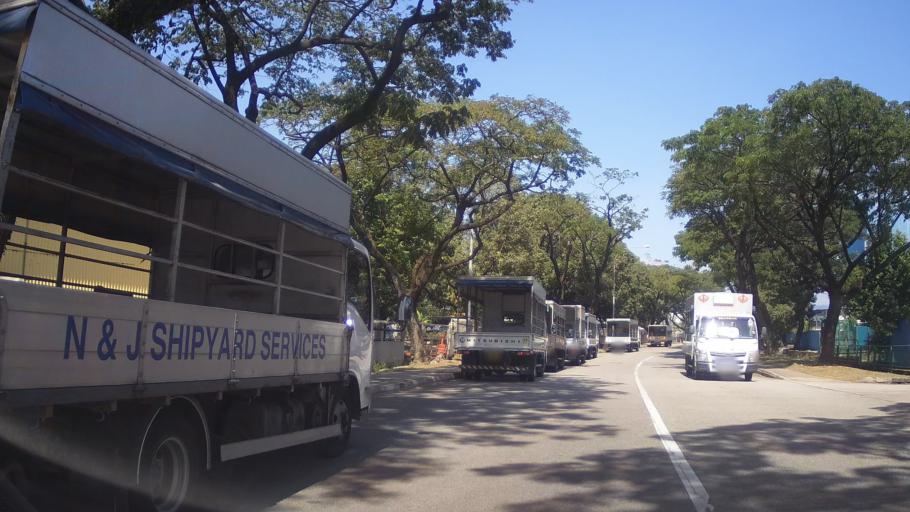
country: SG
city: Singapore
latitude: 1.3050
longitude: 103.7027
